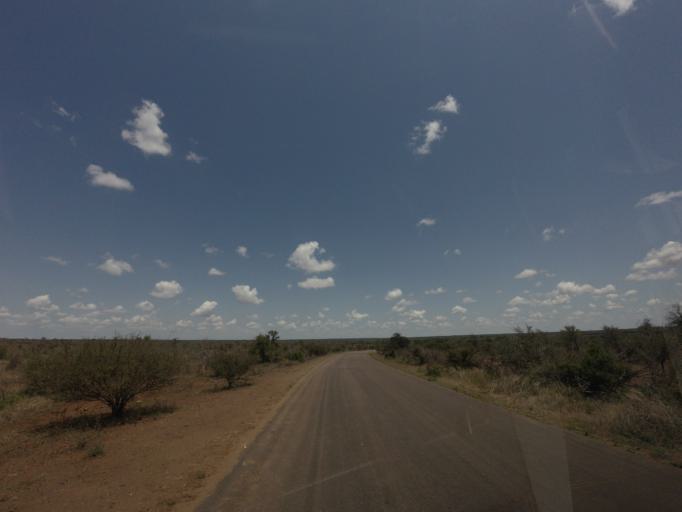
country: ZA
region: Mpumalanga
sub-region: Ehlanzeni District
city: Komatipoort
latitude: -24.8017
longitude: 31.8761
